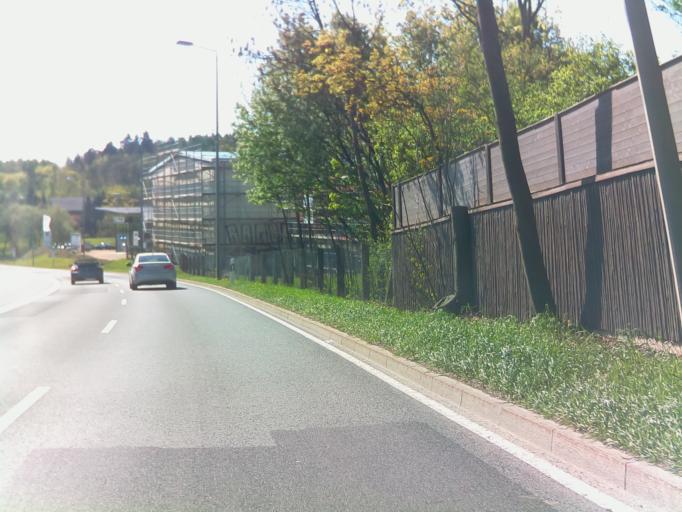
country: DE
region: Saxony
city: Plauen
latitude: 50.5223
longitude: 12.1128
